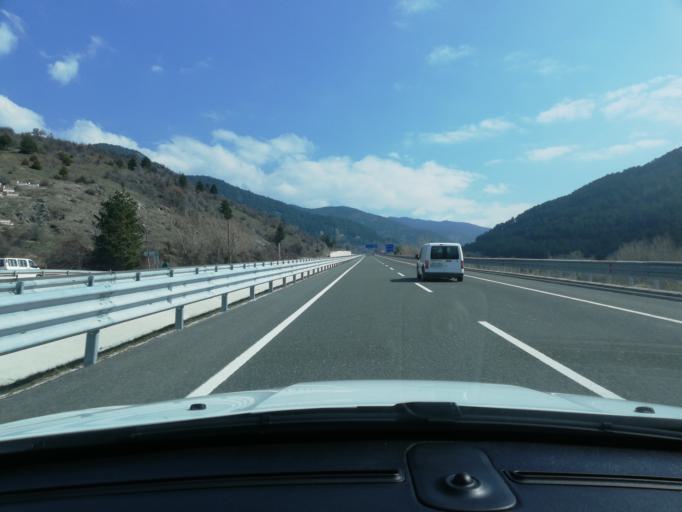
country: TR
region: Cankiri
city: Ilgaz
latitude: 41.0198
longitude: 33.7105
